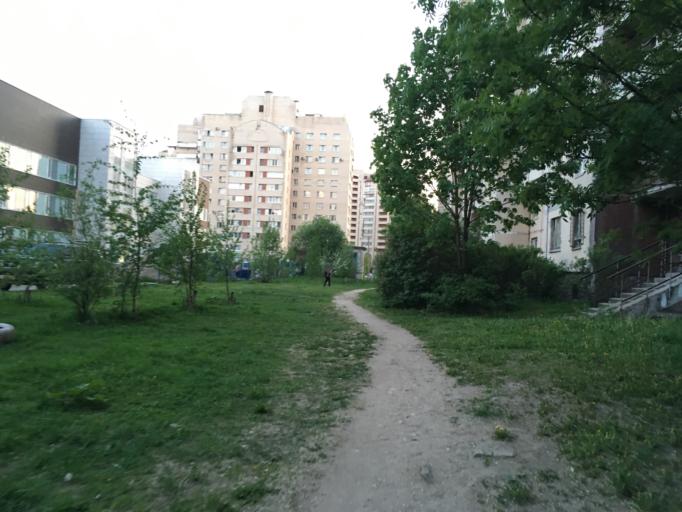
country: RU
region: St.-Petersburg
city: Kolomyagi
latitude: 60.0241
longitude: 30.2902
